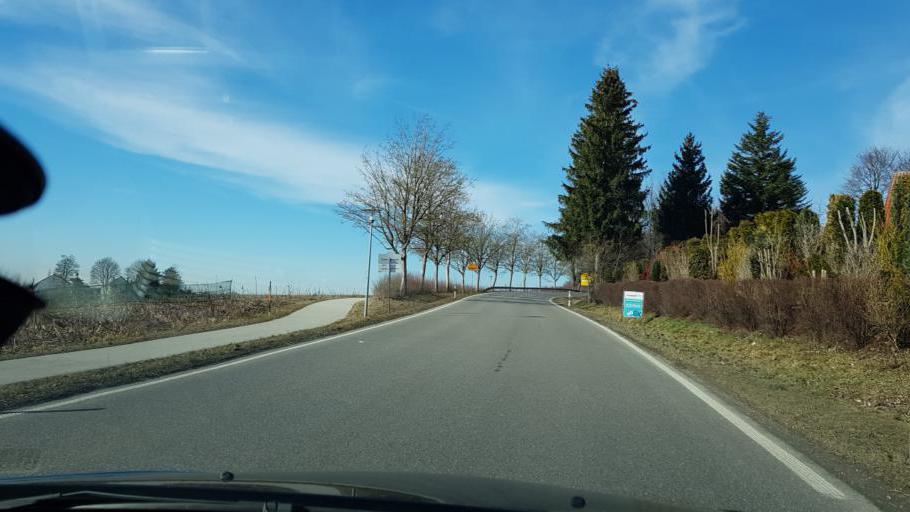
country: DE
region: Bavaria
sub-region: Upper Bavaria
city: Mammendorf
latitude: 48.2077
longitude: 11.1498
